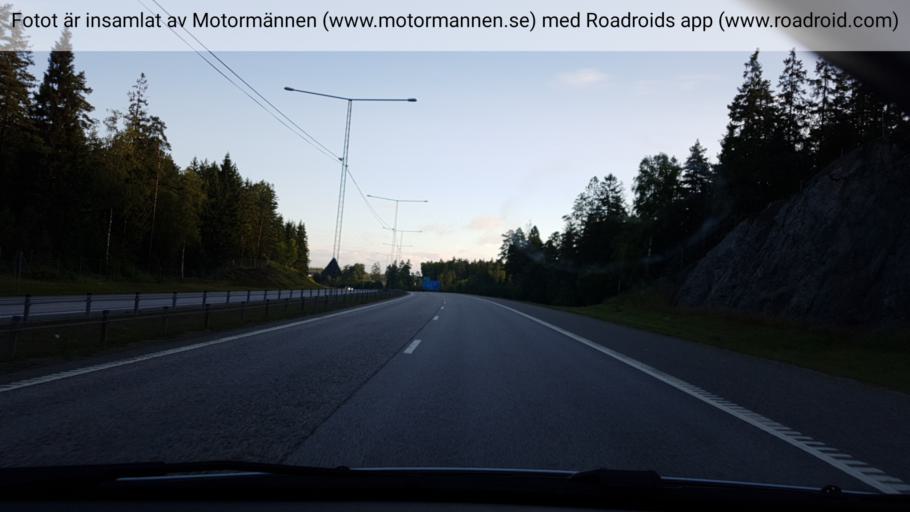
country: SE
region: Stockholm
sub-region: Haninge Kommun
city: Haninge
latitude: 59.1408
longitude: 18.1607
